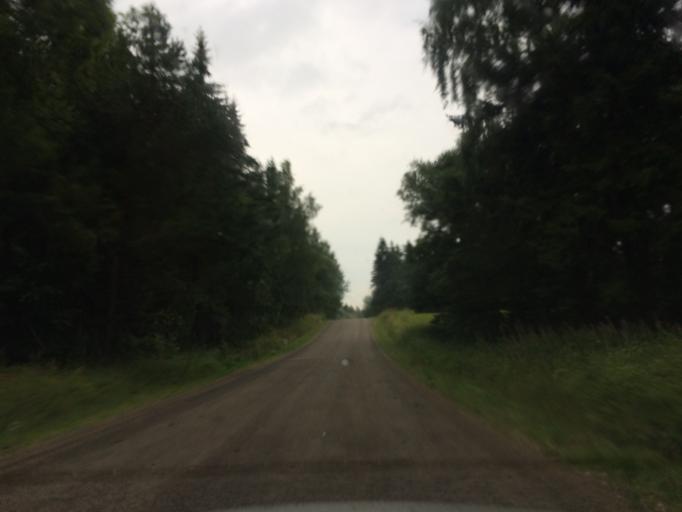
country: LV
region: Rezekne
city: Rezekne
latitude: 56.5695
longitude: 27.4655
